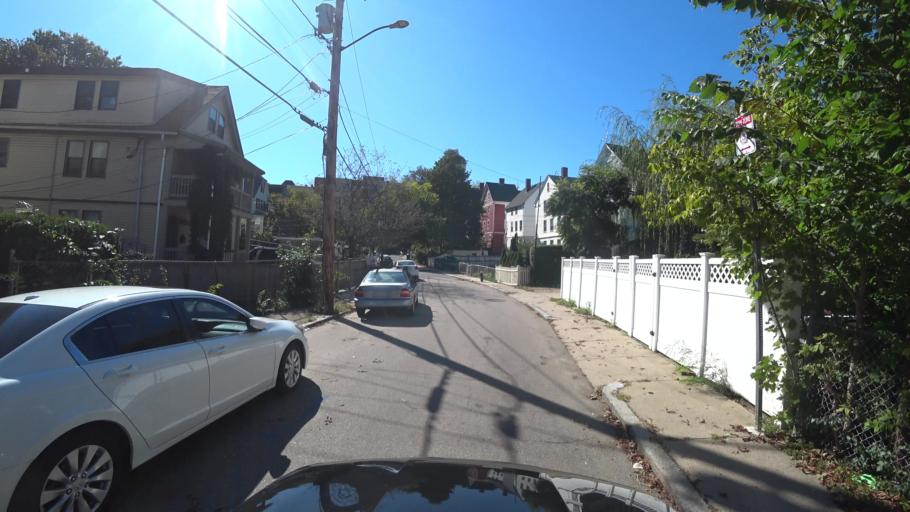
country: US
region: Massachusetts
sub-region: Norfolk County
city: Brookline
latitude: 42.3240
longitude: -71.1049
